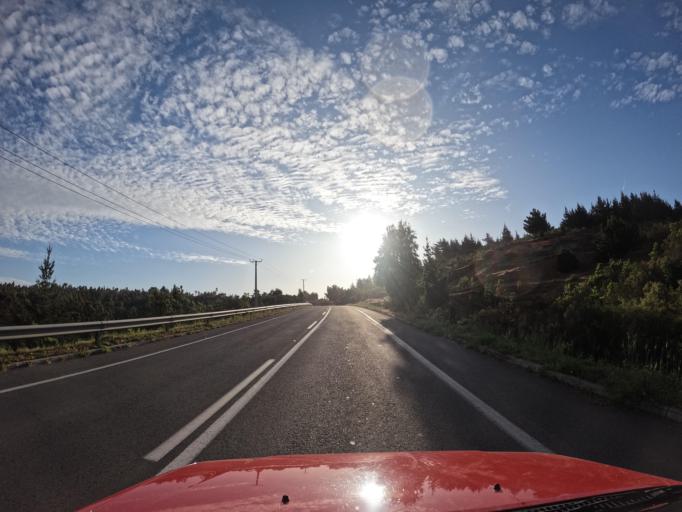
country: CL
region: Valparaiso
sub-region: San Antonio Province
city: San Antonio
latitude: -34.0494
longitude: -71.6168
